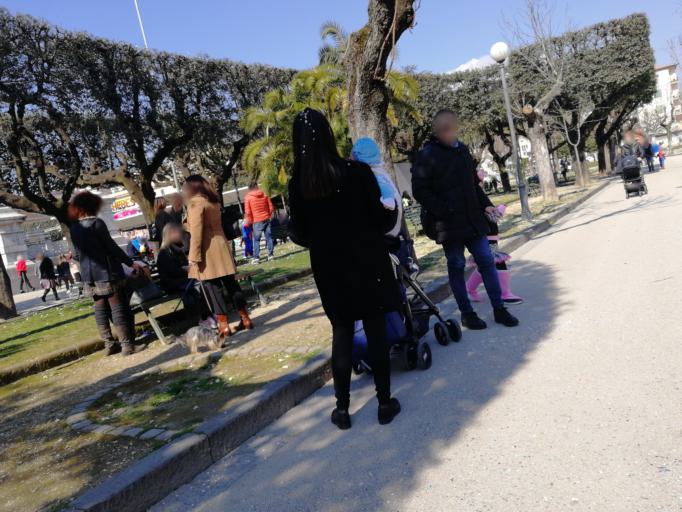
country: IT
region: Campania
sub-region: Provincia di Caserta
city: Santa Maria Capua Vetere
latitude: 41.0849
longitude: 14.2573
